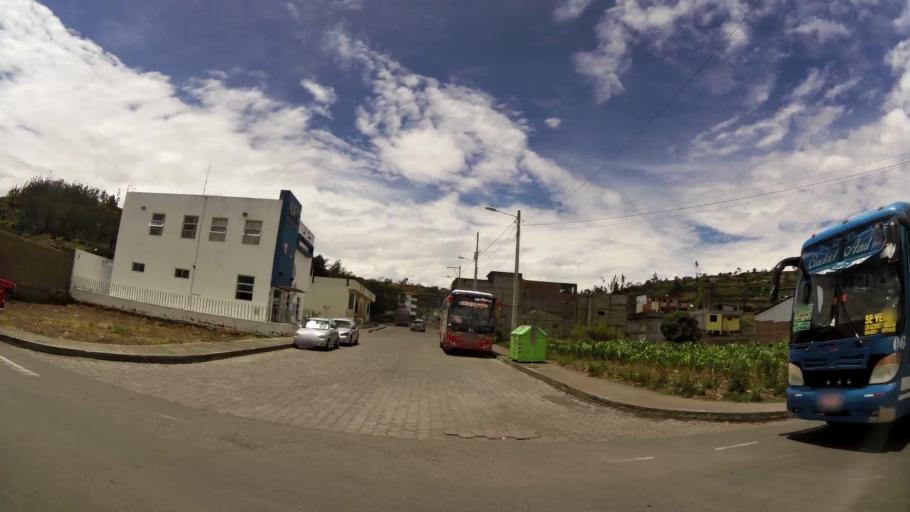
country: EC
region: Tungurahua
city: Pelileo
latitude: -1.3291
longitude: -78.5269
